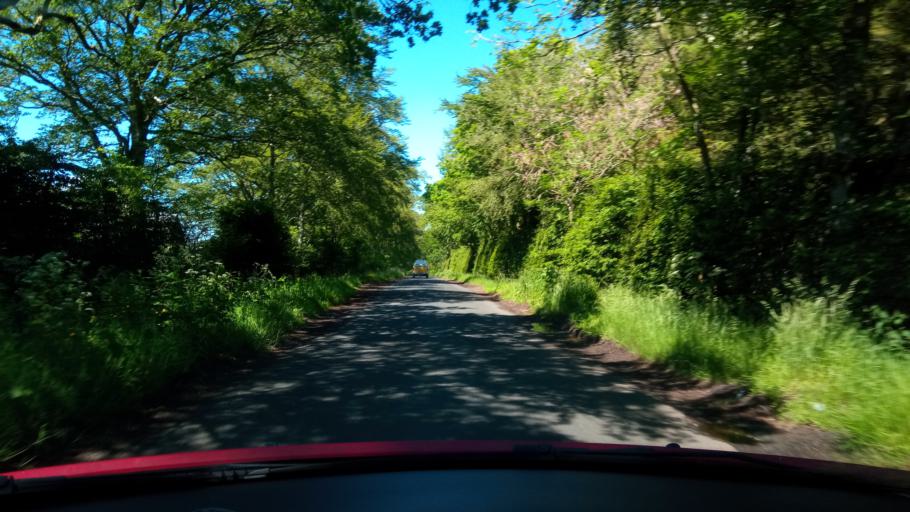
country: GB
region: Scotland
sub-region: The Scottish Borders
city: Duns
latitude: 55.8039
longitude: -2.4858
